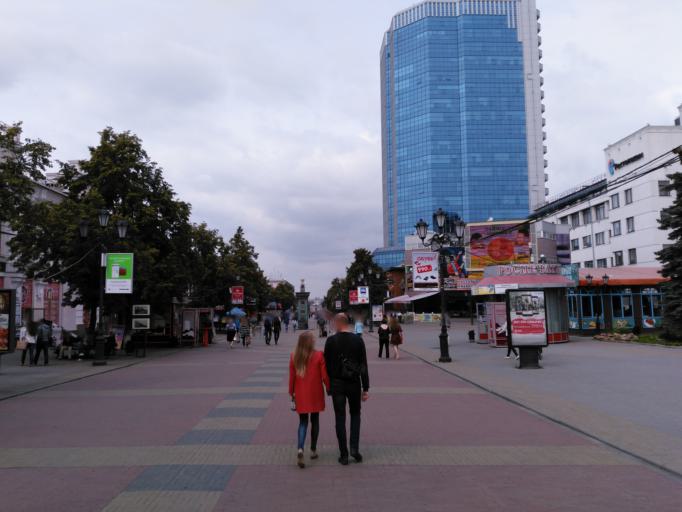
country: RU
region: Chelyabinsk
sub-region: Gorod Chelyabinsk
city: Chelyabinsk
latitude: 55.1636
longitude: 61.4009
